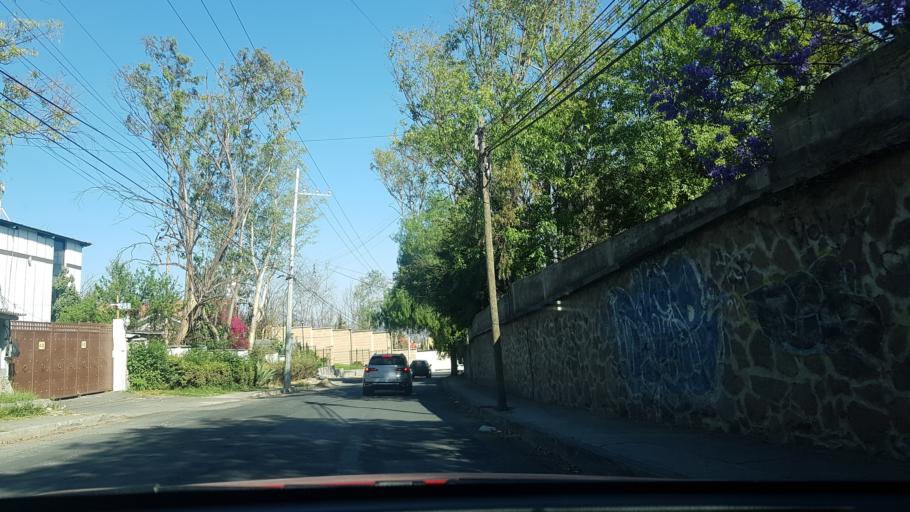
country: MX
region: Mexico
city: Cuautitlan Izcalli
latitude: 19.6260
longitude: -99.2346
